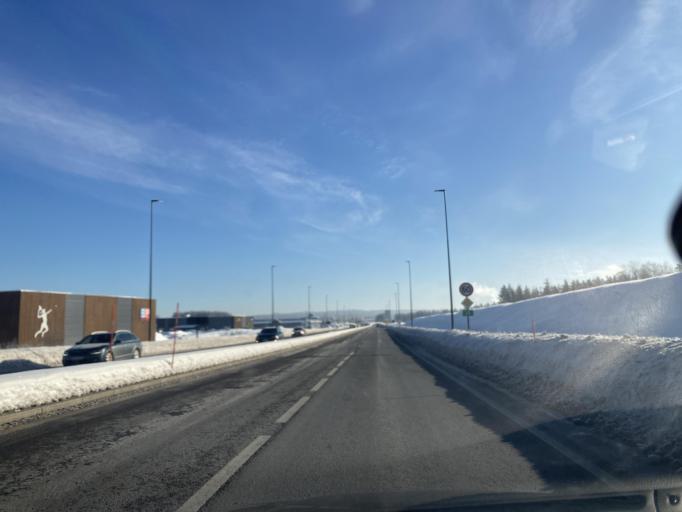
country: NO
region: Hedmark
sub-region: Elverum
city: Elverum
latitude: 60.8862
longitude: 11.5166
